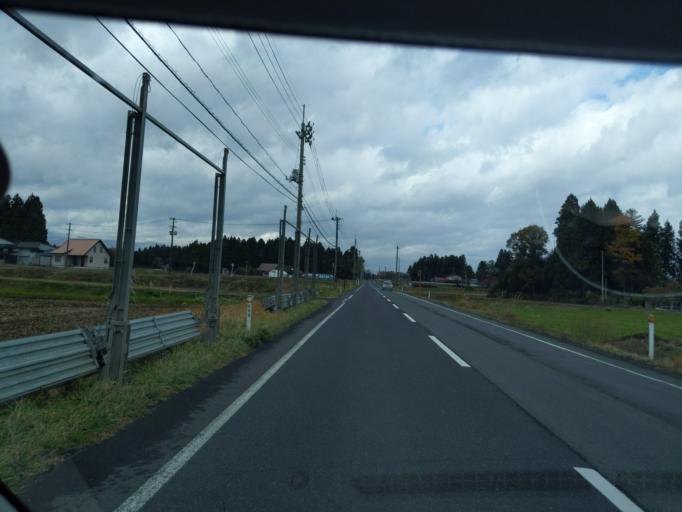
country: JP
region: Iwate
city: Mizusawa
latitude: 39.0753
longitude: 141.0537
